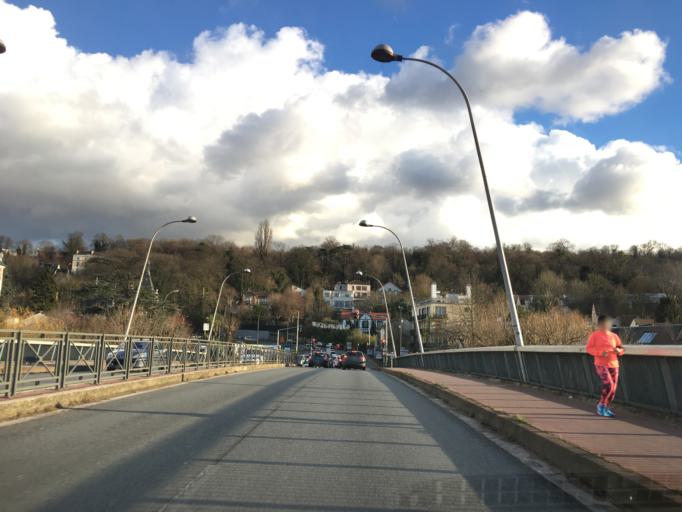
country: FR
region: Ile-de-France
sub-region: Departement du Val-de-Marne
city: Chennevieres-sur-Marne
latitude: 48.7907
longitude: 2.5213
